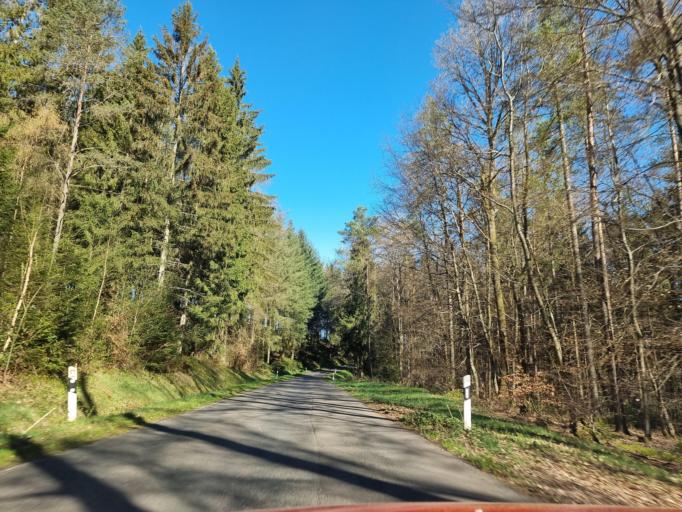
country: DE
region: Rheinland-Pfalz
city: Dierscheid
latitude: 49.8936
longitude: 6.7642
